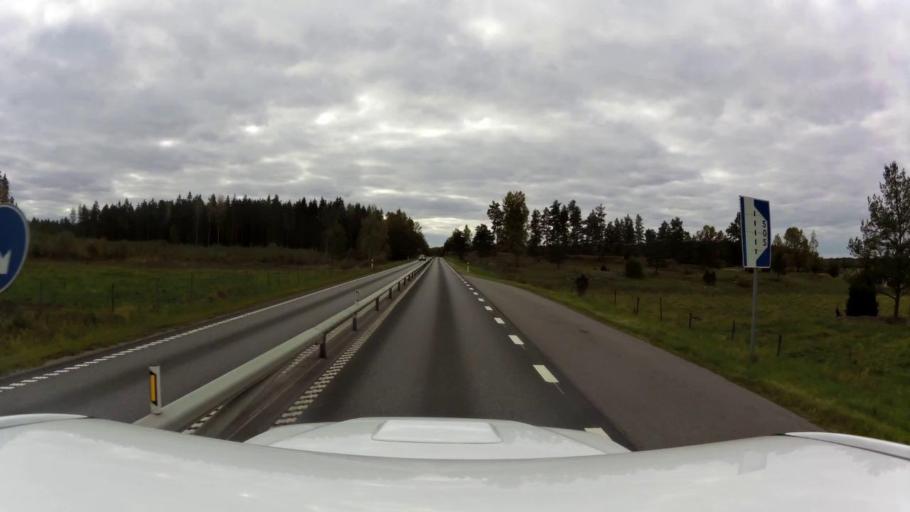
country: SE
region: OEstergoetland
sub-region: Linkopings Kommun
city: Malmslatt
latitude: 58.3004
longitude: 15.5639
